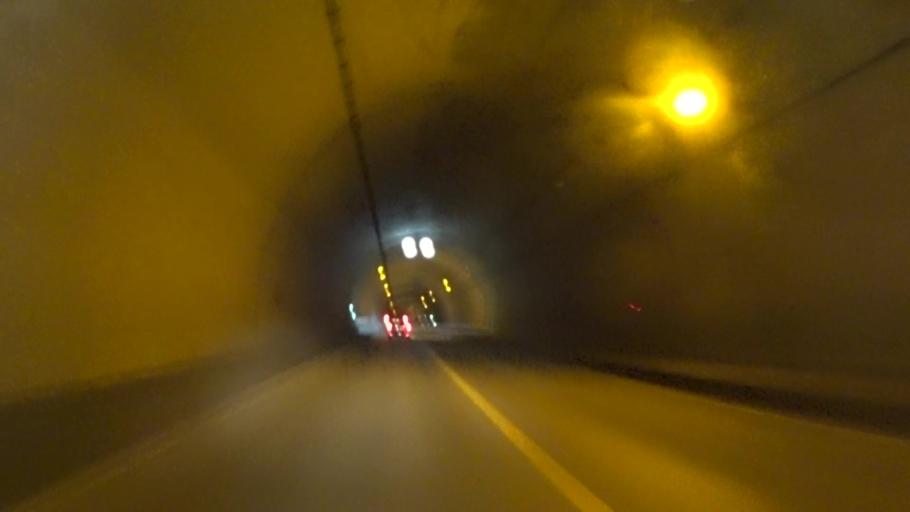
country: JP
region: Kyoto
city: Fukuchiyama
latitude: 35.4074
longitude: 135.0383
